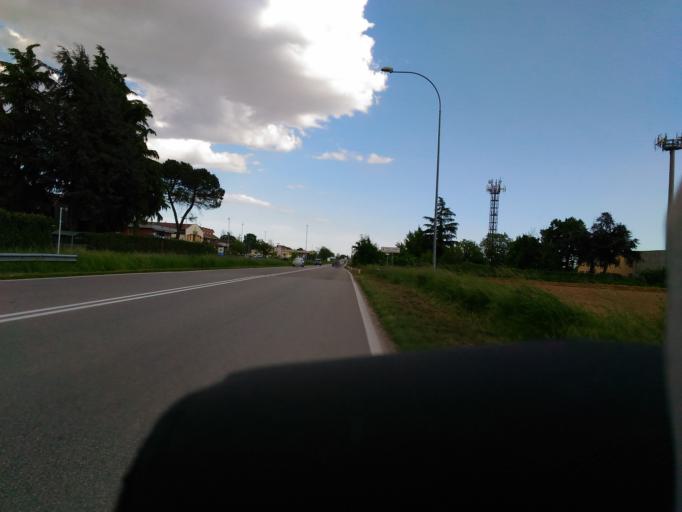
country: IT
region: Lombardy
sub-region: Citta metropolitana di Milano
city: Mediglia
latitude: 45.3958
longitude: 9.3269
